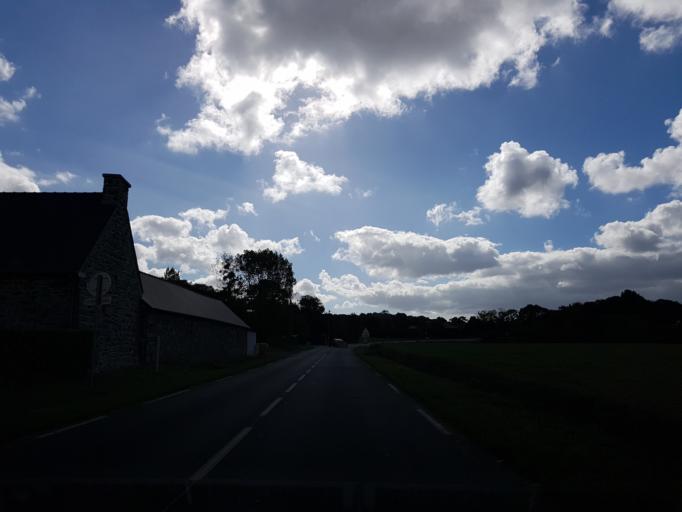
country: FR
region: Brittany
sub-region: Departement des Cotes-d'Armor
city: Yffiniac
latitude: 48.4663
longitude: -2.6985
